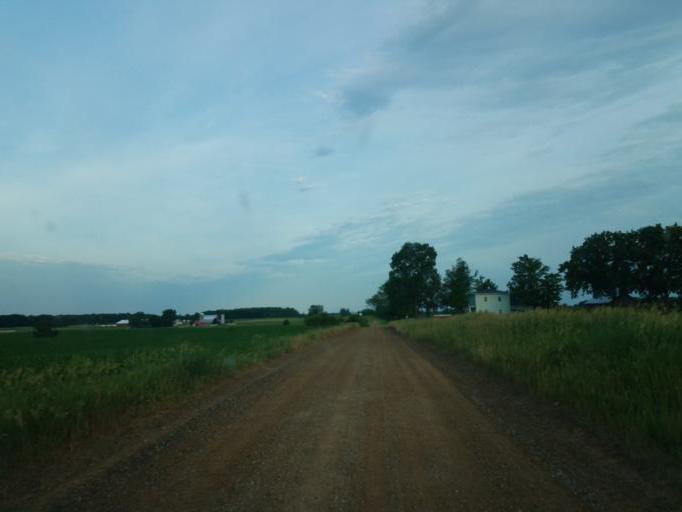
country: US
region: Michigan
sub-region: Eaton County
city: Charlotte
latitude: 42.5973
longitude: -84.9281
